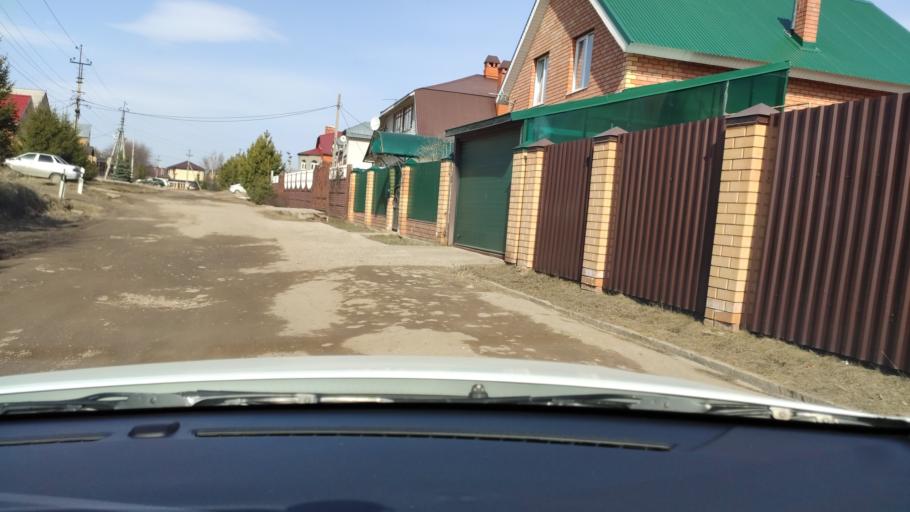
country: RU
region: Tatarstan
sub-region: Gorod Kazan'
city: Kazan
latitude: 55.7854
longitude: 49.2478
